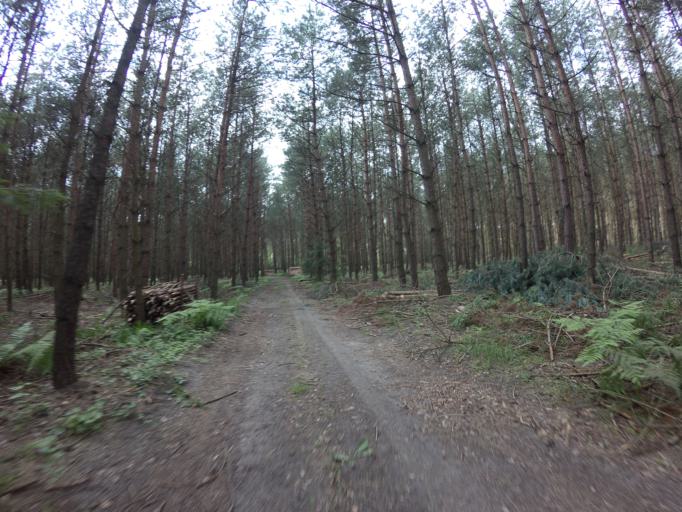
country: PL
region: Kujawsko-Pomorskie
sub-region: Powiat bydgoski
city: Koronowo
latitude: 53.3760
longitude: 17.9934
